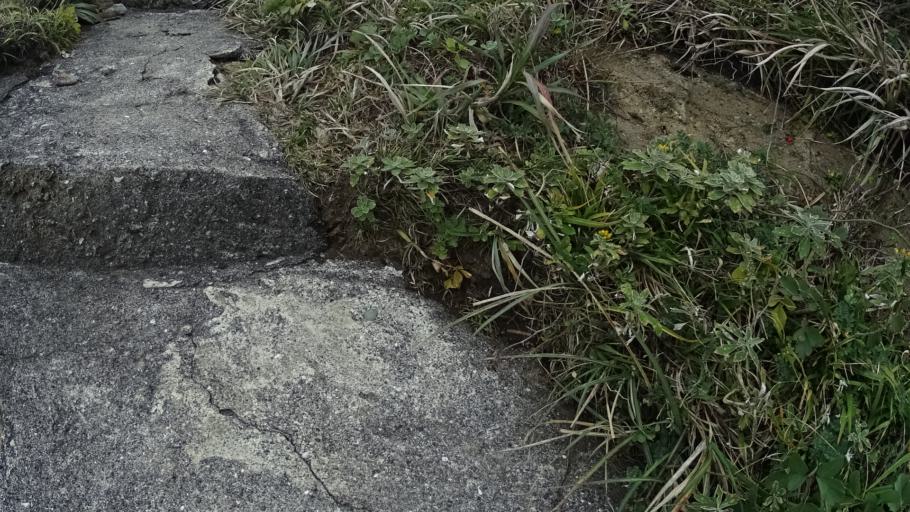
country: JP
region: Kanagawa
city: Miura
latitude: 35.1633
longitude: 139.6111
